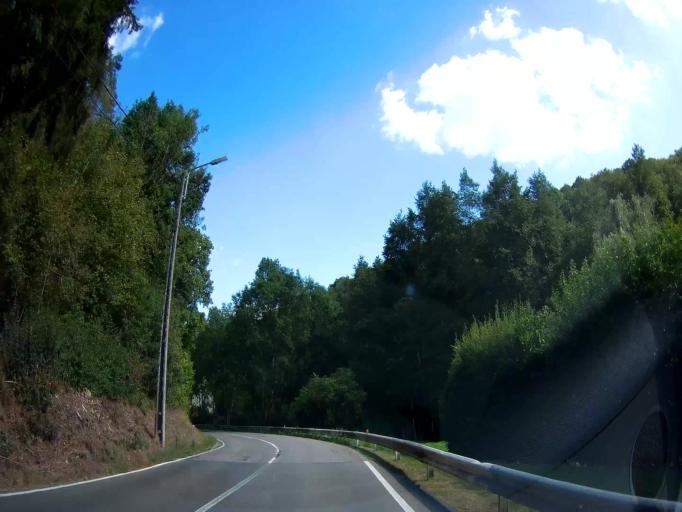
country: BE
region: Wallonia
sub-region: Province de Namur
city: Houyet
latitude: 50.2201
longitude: 4.9815
